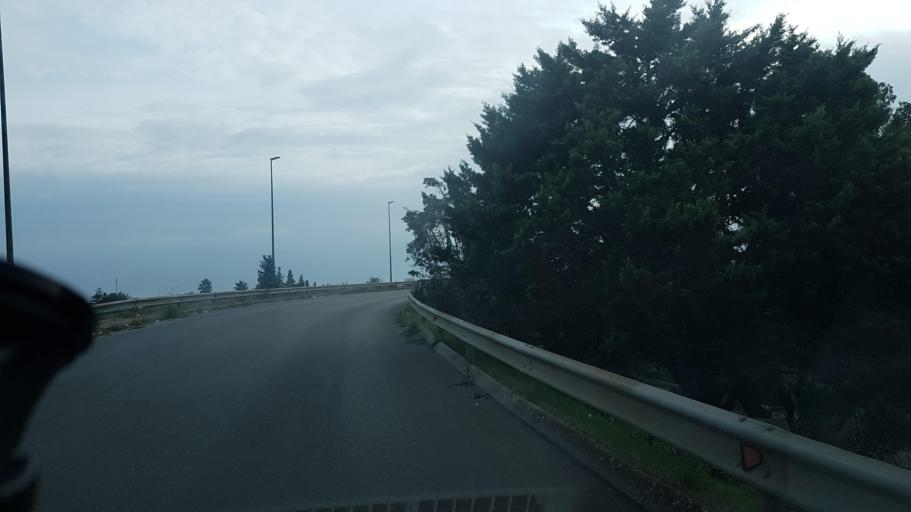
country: IT
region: Apulia
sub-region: Provincia di Lecce
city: Trepuzzi
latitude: 40.4141
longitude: 18.0740
